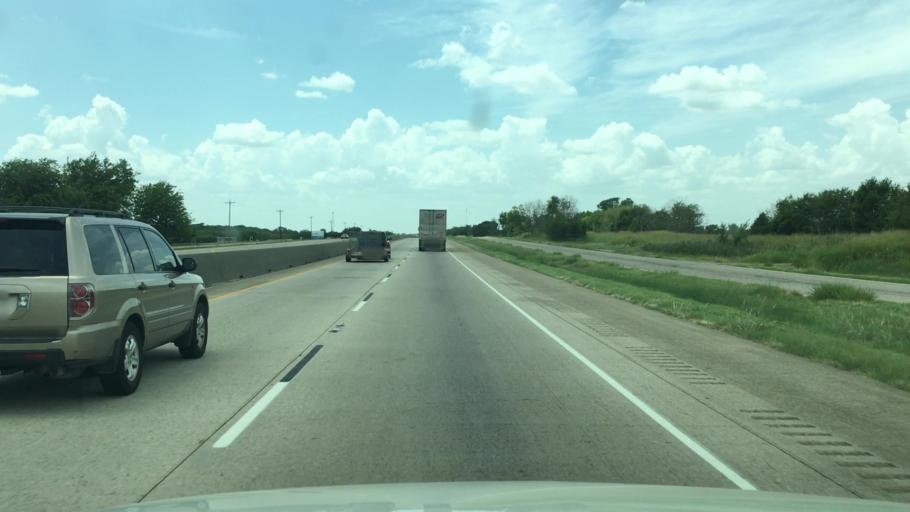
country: US
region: Texas
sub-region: Hopkins County
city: Sulphur Springs
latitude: 33.1299
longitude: -95.7724
